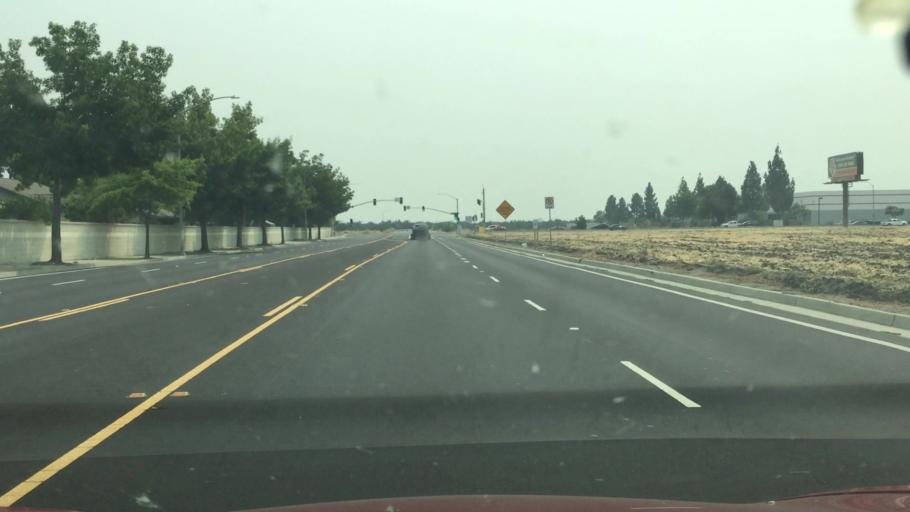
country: US
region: California
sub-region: San Joaquin County
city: Morada
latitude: 38.0231
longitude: -121.2642
